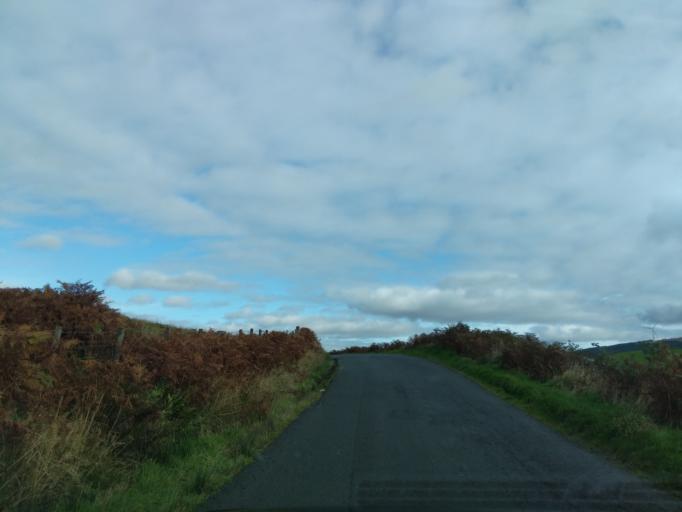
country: GB
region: Scotland
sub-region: Dumfries and Galloway
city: Castle Douglas
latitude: 55.1170
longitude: -4.0915
